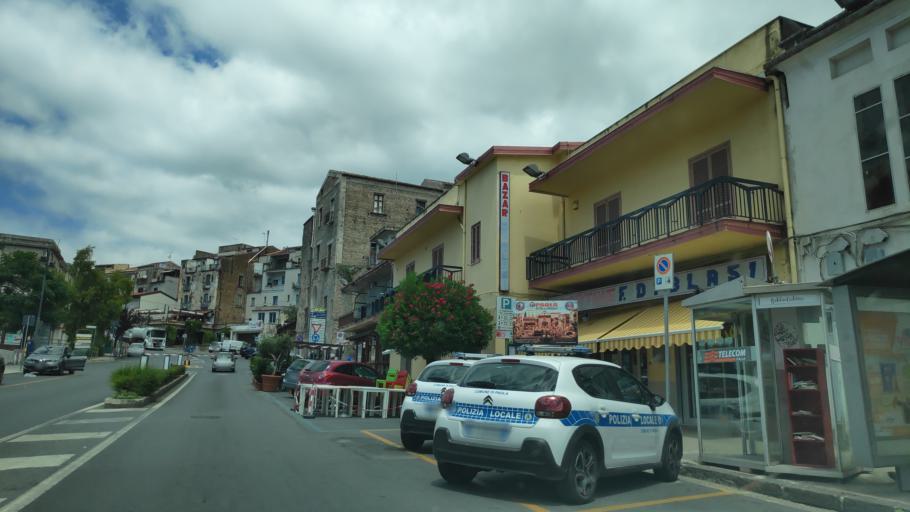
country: IT
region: Calabria
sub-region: Provincia di Cosenza
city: Paola
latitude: 39.3595
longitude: 16.0411
